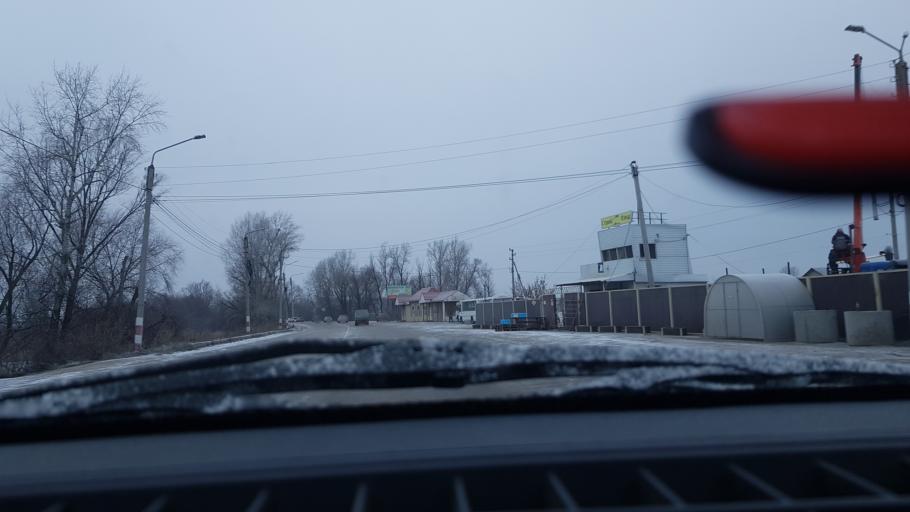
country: RU
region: Ulyanovsk
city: Dimitrovgrad
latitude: 54.1866
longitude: 49.6544
